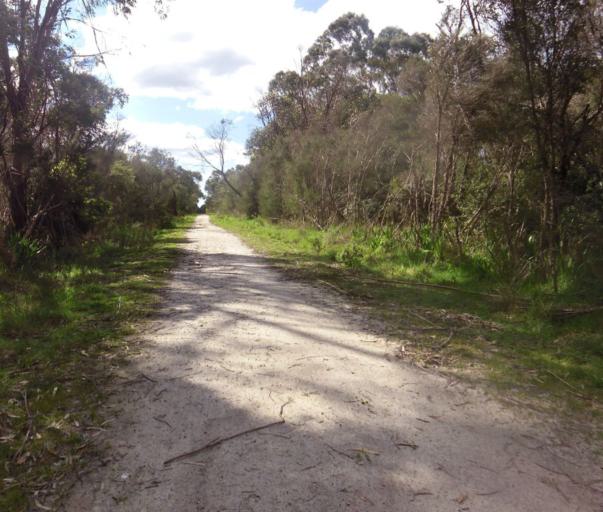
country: AU
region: Victoria
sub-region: Bass Coast
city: North Wonthaggi
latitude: -38.6453
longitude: 146.0312
